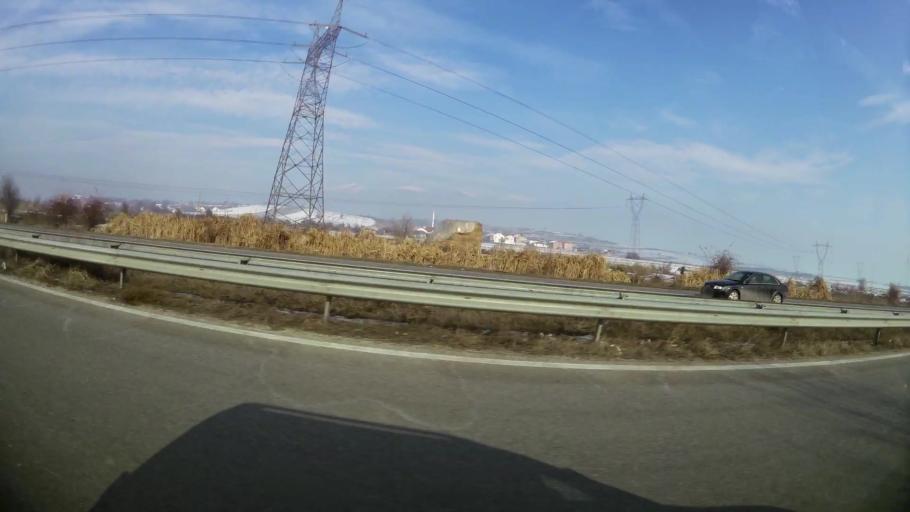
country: MK
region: Butel
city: Butel
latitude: 42.0389
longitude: 21.4633
